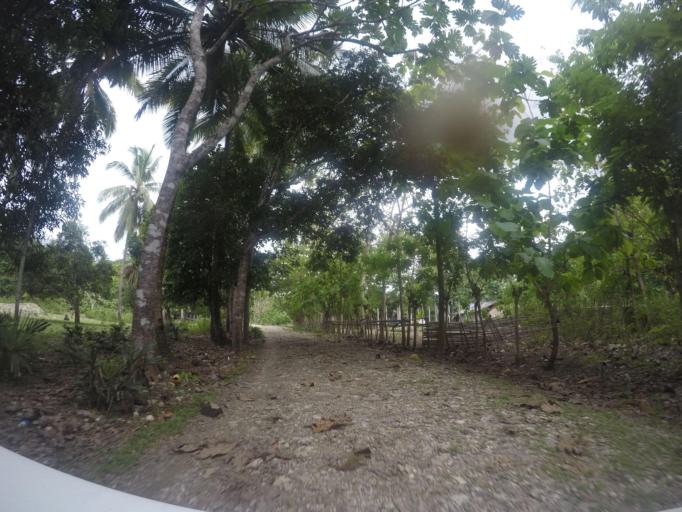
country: TL
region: Viqueque
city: Viqueque
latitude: -8.8536
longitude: 126.3547
